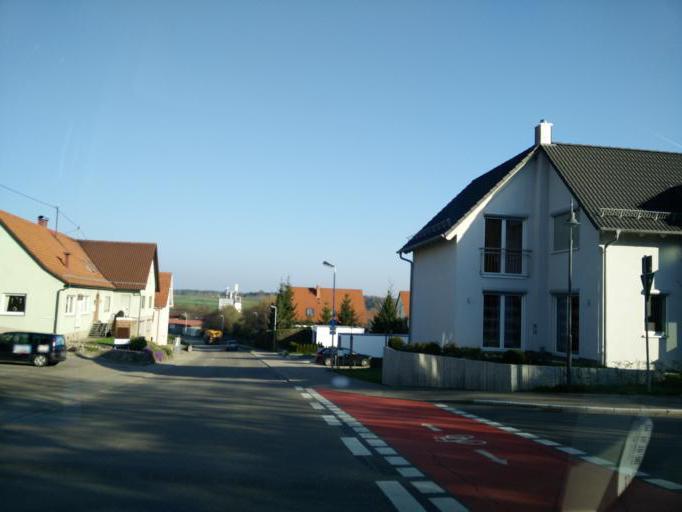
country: DE
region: Baden-Wuerttemberg
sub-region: Regierungsbezirk Stuttgart
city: Deckenpfronn
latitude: 48.6499
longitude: 8.8182
